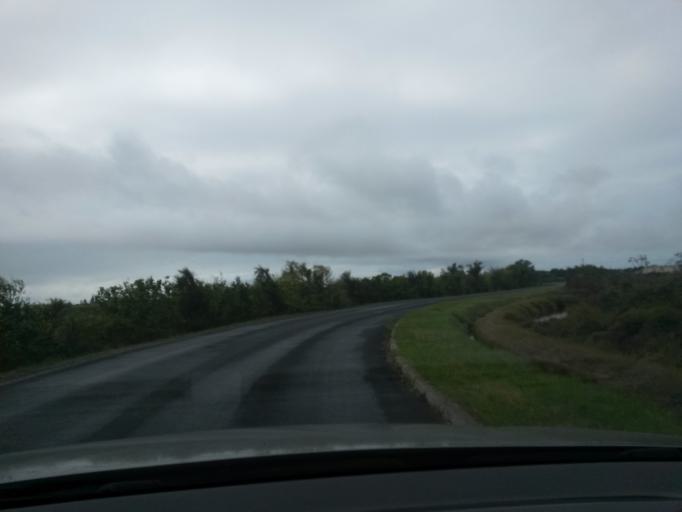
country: FR
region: Poitou-Charentes
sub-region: Departement de la Charente-Maritime
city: Saint-Trojan-les-Bains
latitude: 45.8776
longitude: -1.1992
